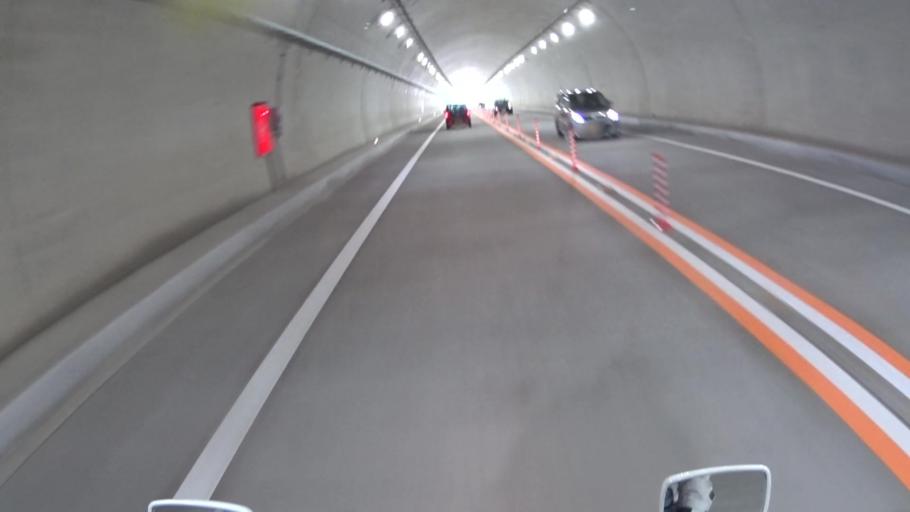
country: JP
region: Hyogo
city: Sasayama
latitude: 35.1530
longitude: 135.4200
